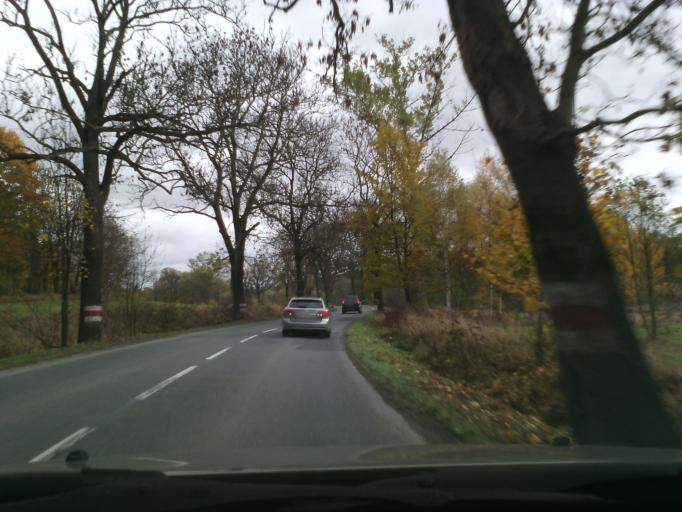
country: PL
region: Lower Silesian Voivodeship
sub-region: Powiat kamiennogorski
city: Kamienna Gora
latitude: 50.7757
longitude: 15.9920
